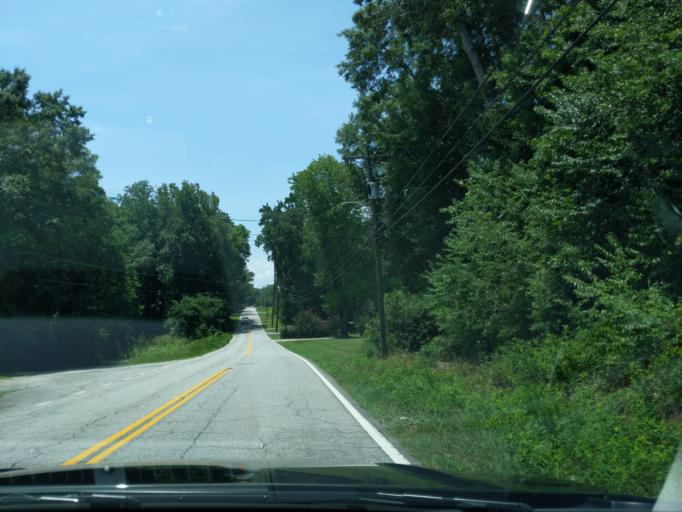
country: US
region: South Carolina
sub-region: Laurens County
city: Laurens
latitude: 34.4868
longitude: -82.0228
